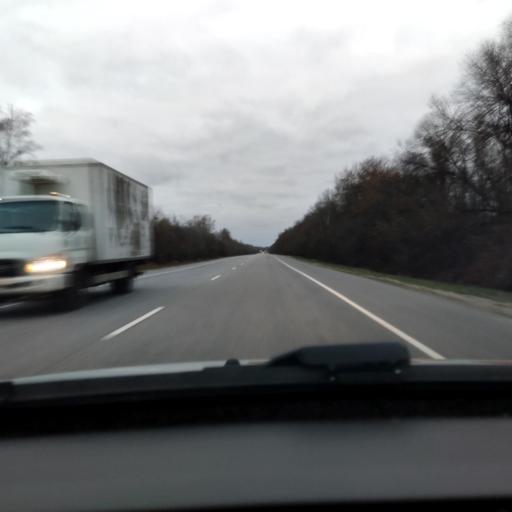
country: RU
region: Lipetsk
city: Khlevnoye
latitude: 52.3559
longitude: 39.1968
